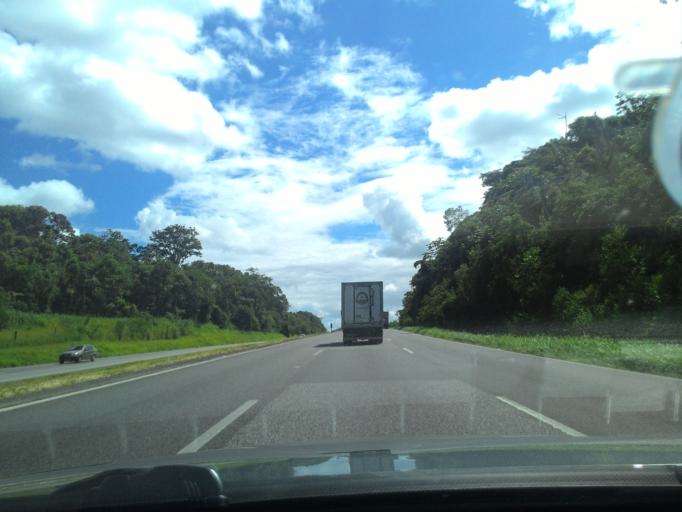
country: BR
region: Sao Paulo
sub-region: Pariquera-Acu
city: Pariquera Acu
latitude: -24.6086
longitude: -47.8811
